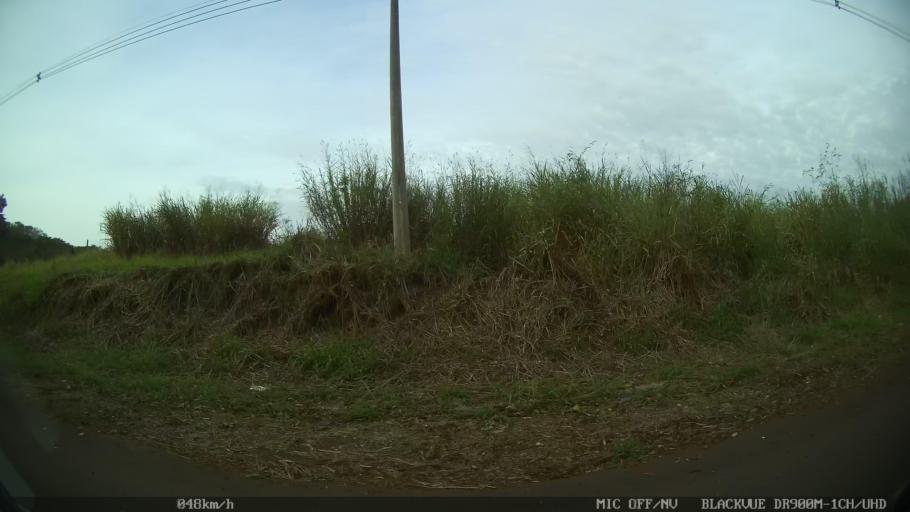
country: BR
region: Sao Paulo
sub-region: Piracicaba
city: Piracicaba
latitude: -22.6915
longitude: -47.5821
